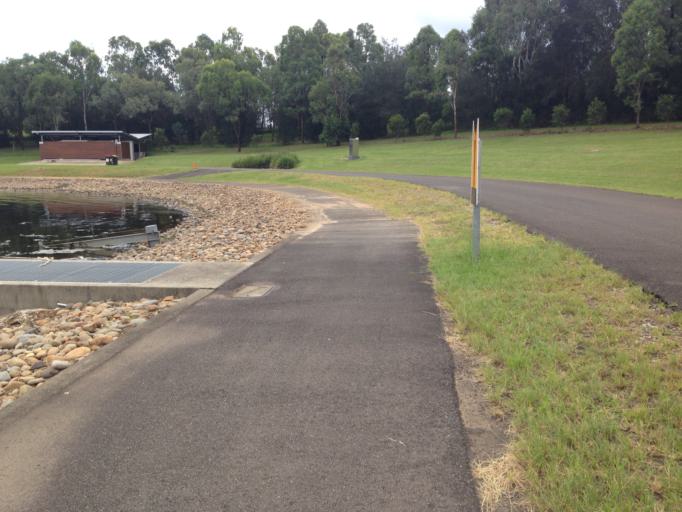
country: AU
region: New South Wales
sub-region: Penrith Municipality
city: Penrith
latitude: -33.7250
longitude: 150.6929
